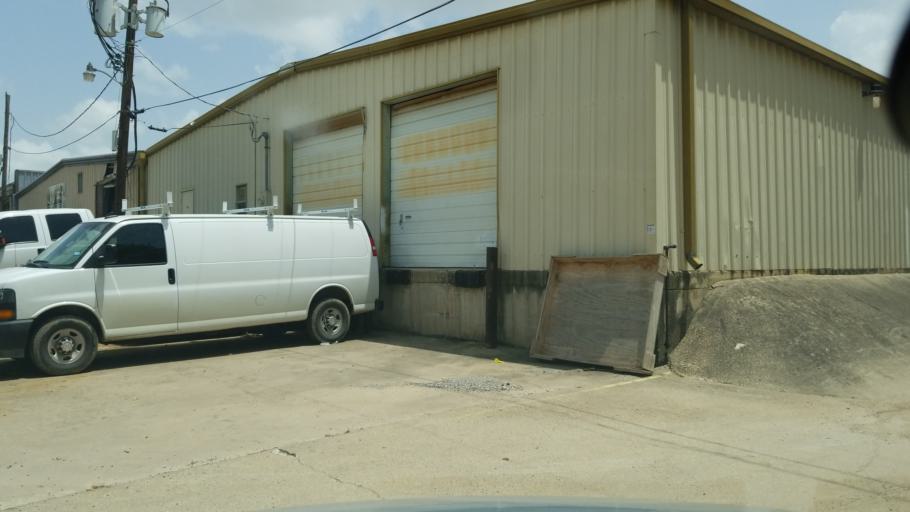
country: US
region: Texas
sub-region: Dallas County
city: Irving
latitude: 32.8260
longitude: -96.9076
